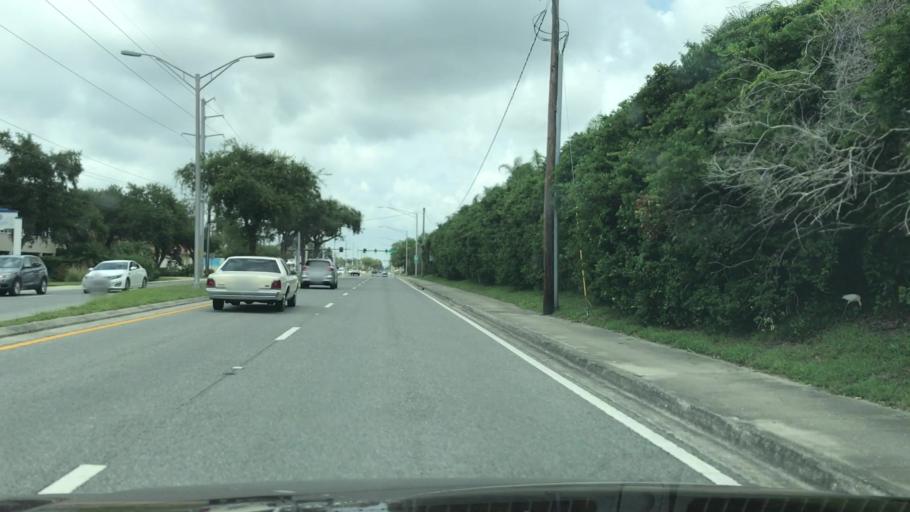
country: US
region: Florida
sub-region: Sarasota County
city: Gulf Gate Estates
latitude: 27.2520
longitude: -82.4975
